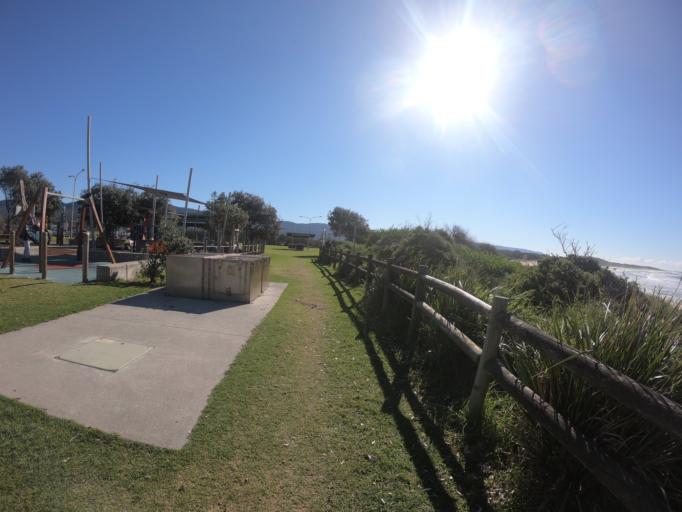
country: AU
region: New South Wales
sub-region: Wollongong
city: East Corrimal
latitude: -34.3850
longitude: 150.9151
